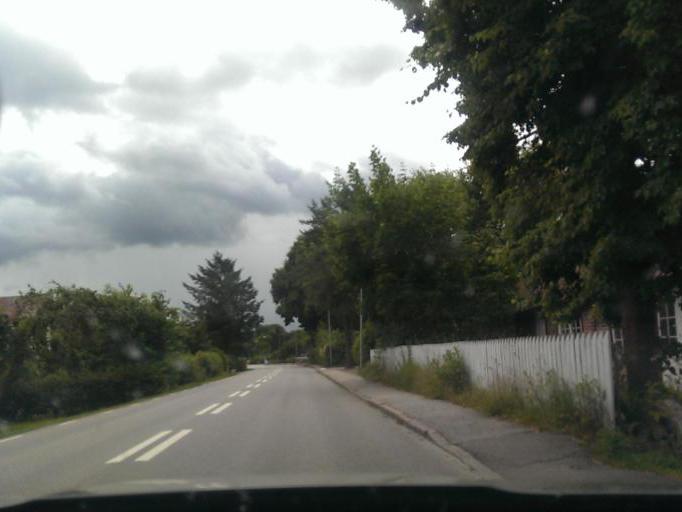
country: SE
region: Skane
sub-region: Eslovs Kommun
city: Stehag
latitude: 55.9665
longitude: 13.3278
